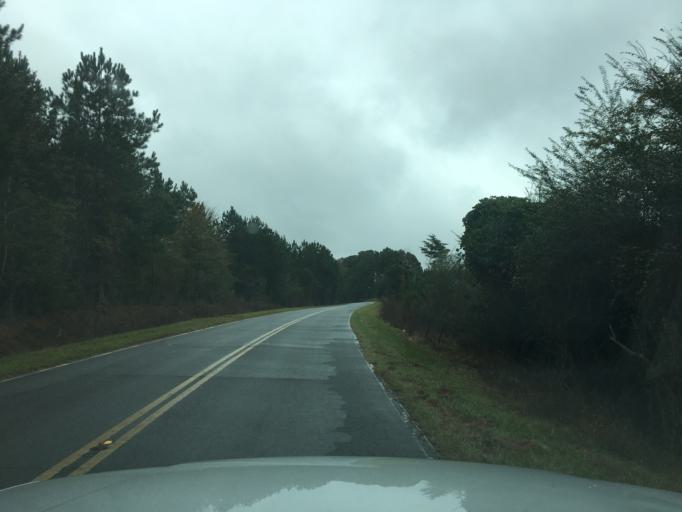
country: US
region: South Carolina
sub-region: Pickens County
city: Central
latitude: 34.7478
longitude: -82.7725
